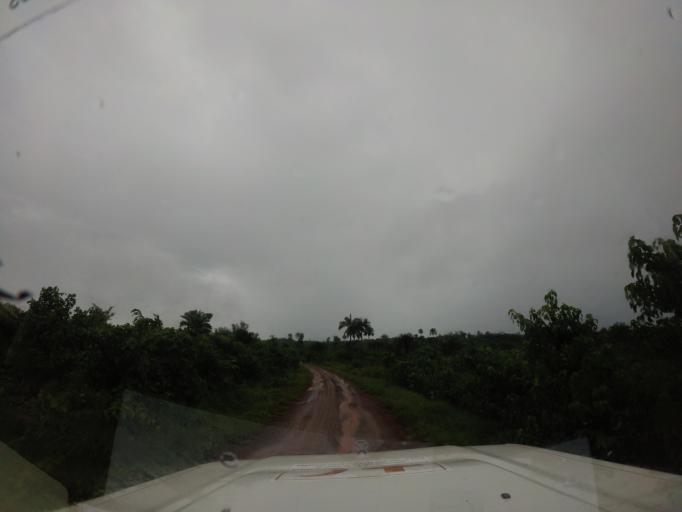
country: SL
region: Eastern Province
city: Kenema
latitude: 7.7375
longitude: -11.1911
